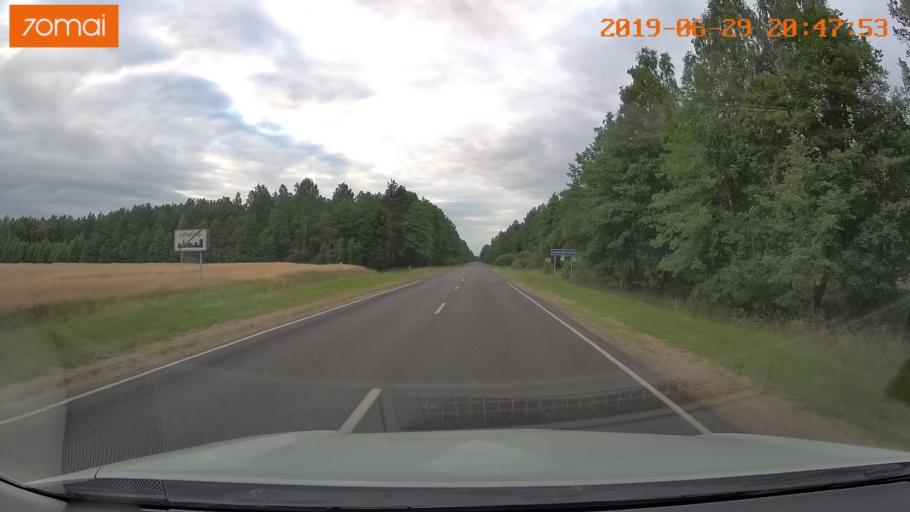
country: BY
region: Brest
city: Hantsavichy
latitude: 52.6435
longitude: 26.3164
